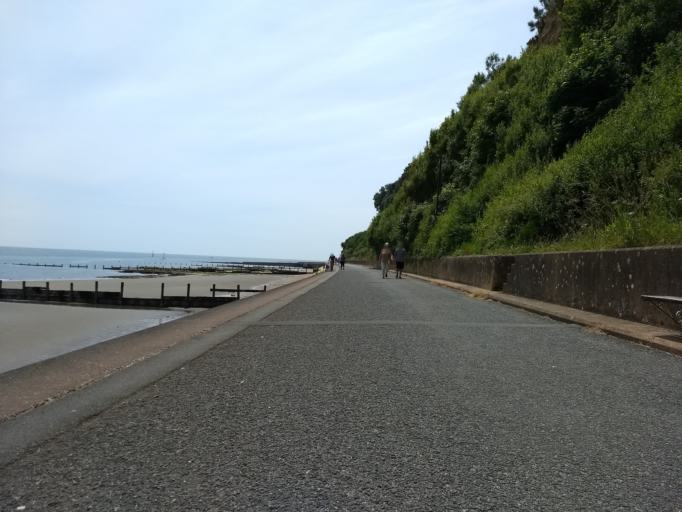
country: GB
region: England
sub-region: Isle of Wight
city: Sandown
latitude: 50.6389
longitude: -1.1690
